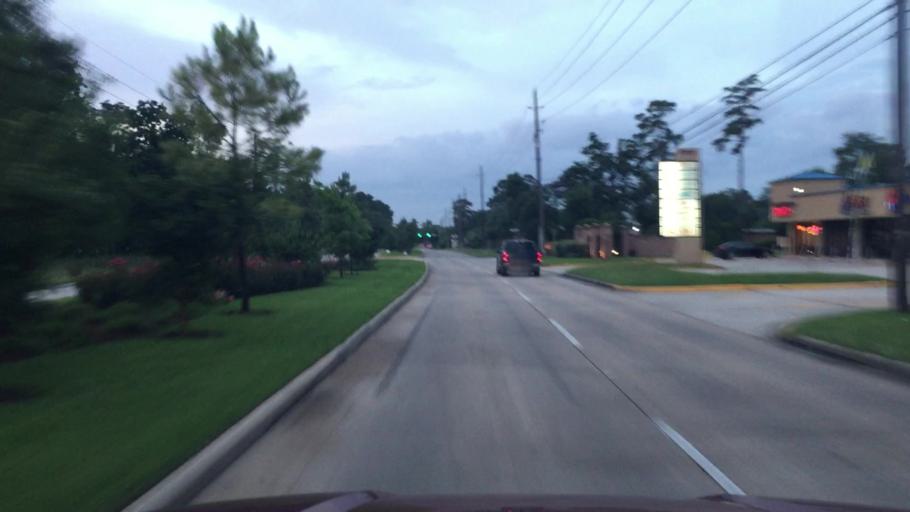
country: US
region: Texas
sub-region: Harris County
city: Tomball
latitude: 30.0330
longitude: -95.5345
